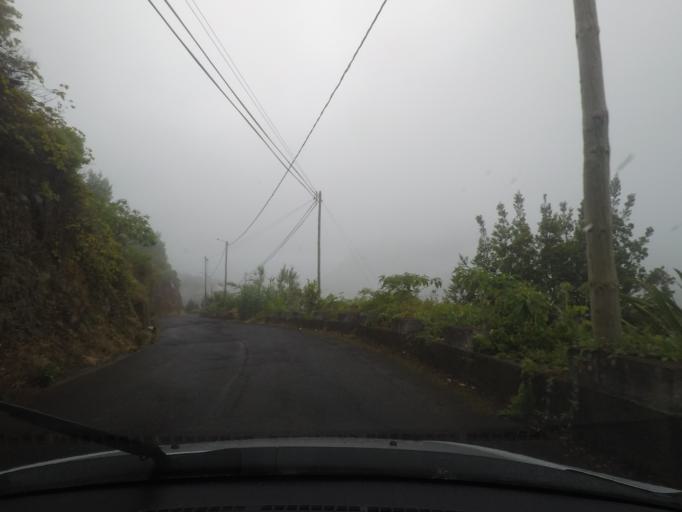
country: PT
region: Madeira
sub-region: Santana
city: Santana
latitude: 32.7785
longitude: -16.8633
